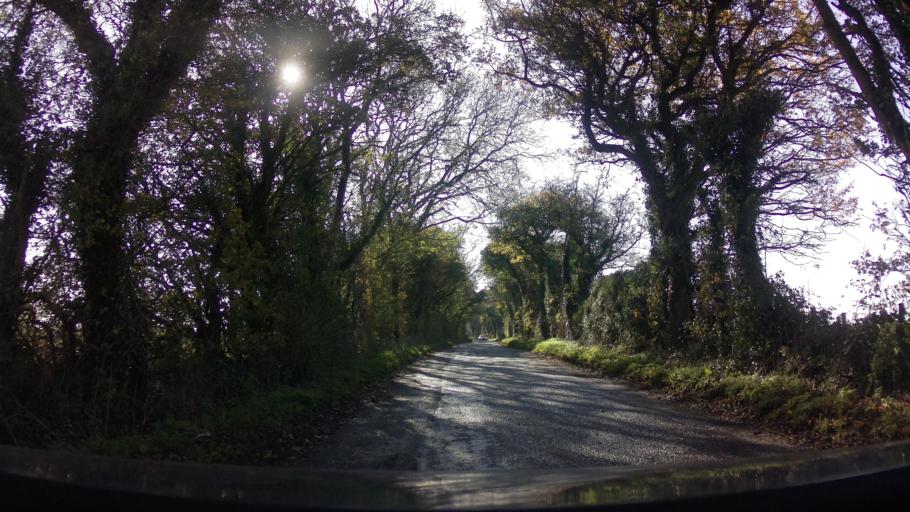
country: GB
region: England
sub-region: Somerset
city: Milborne Port
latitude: 51.0163
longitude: -2.5050
